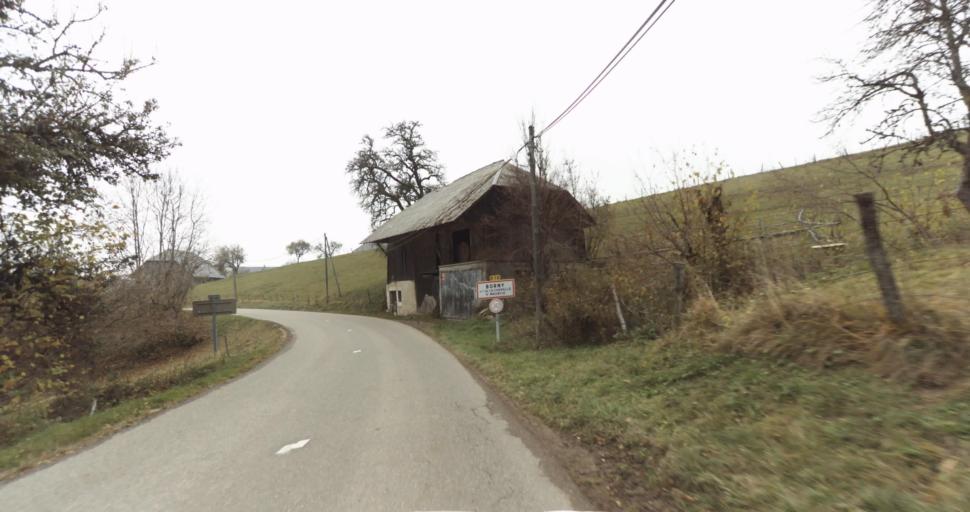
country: FR
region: Rhone-Alpes
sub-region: Departement de la Haute-Savoie
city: Saint-Jorioz
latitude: 45.7733
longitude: 6.1471
